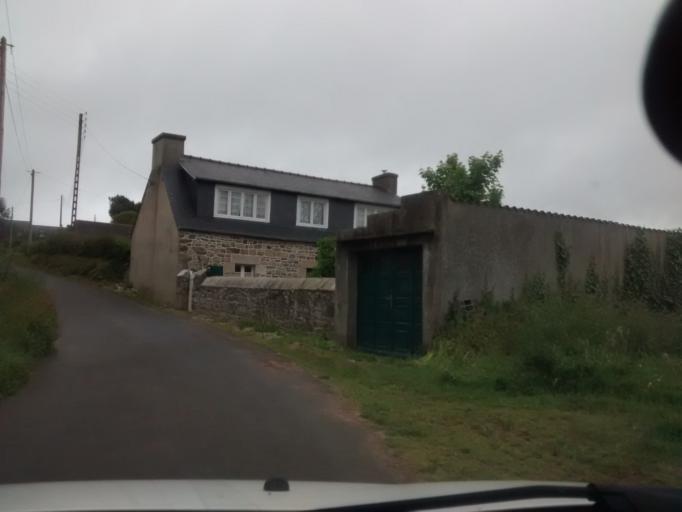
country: FR
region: Brittany
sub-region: Departement des Cotes-d'Armor
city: Plougrescant
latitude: 48.8443
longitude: -3.2145
